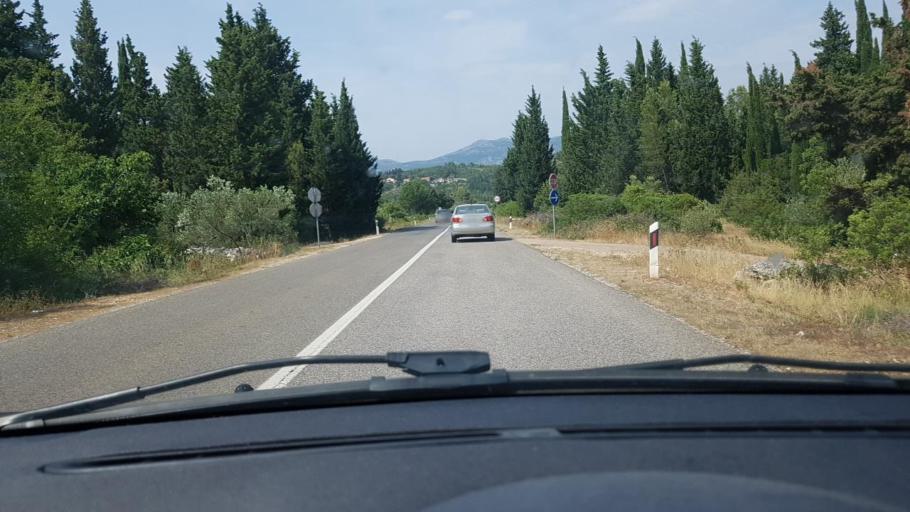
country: HR
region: Dubrovacko-Neretvanska
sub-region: Grad Korcula
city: Zrnovo
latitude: 42.9410
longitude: 17.1048
